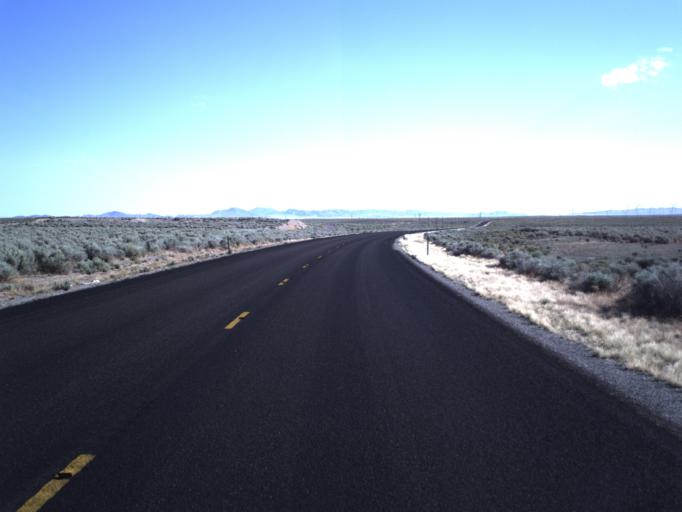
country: US
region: Utah
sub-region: Beaver County
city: Milford
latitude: 38.4426
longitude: -113.0097
